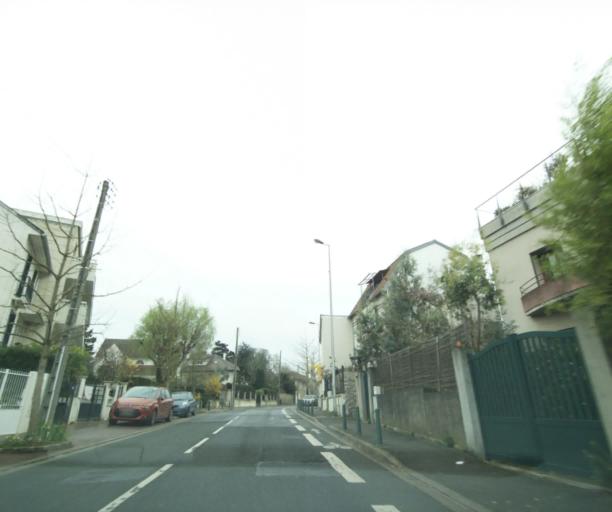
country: FR
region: Ile-de-France
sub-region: Departement des Hauts-de-Seine
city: Clamart
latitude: 48.8090
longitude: 2.2520
